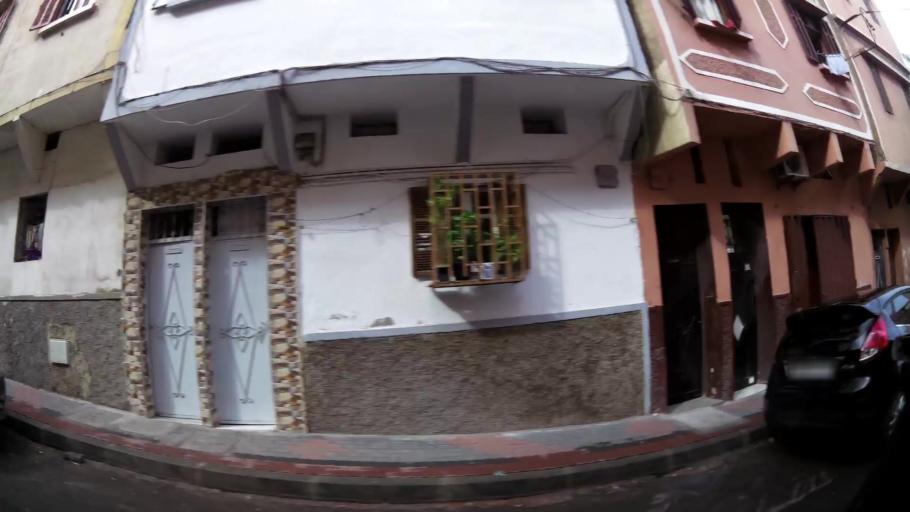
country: MA
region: Grand Casablanca
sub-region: Casablanca
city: Casablanca
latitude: 33.5711
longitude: -7.5863
